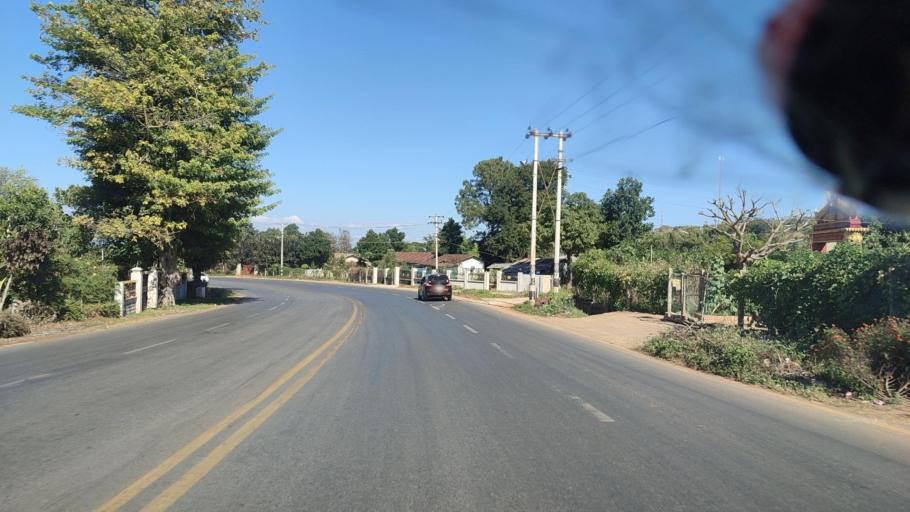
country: MM
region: Mandalay
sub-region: Pyin Oo Lwin District
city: Pyin Oo Lwin
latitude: 22.0689
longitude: 96.5774
